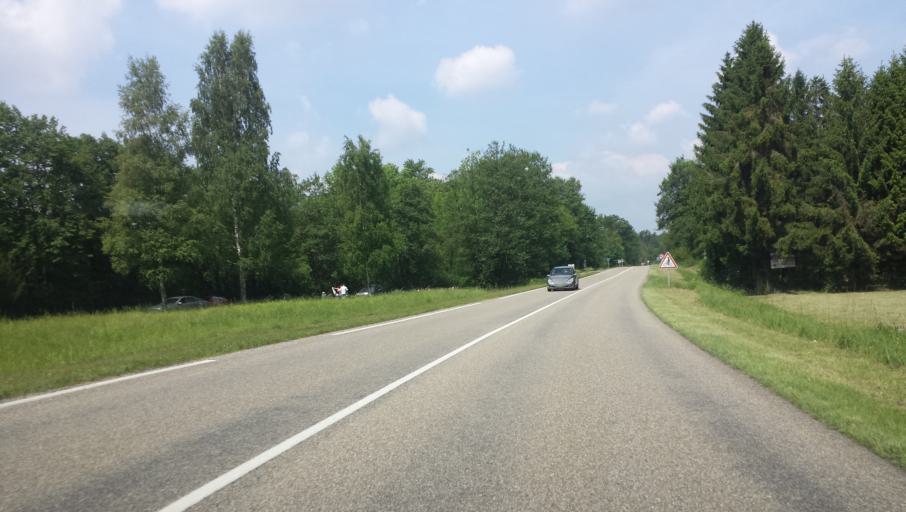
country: DE
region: Rheinland-Pfalz
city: Steinfeld
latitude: 48.9957
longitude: 8.0696
